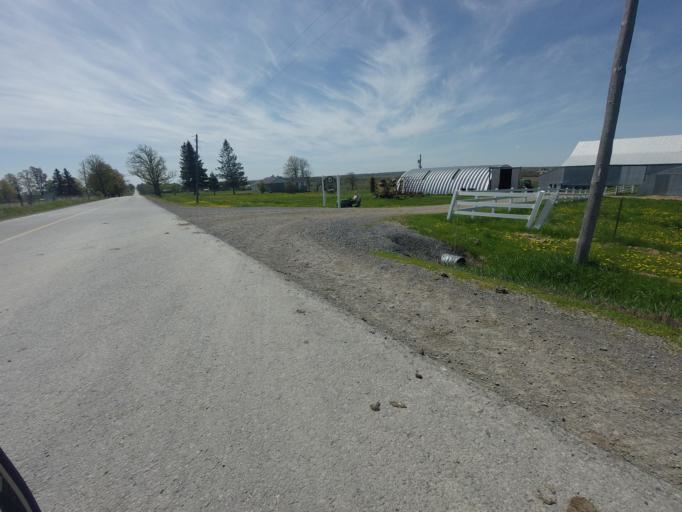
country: CA
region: Ontario
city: Arnprior
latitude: 45.3966
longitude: -76.1479
